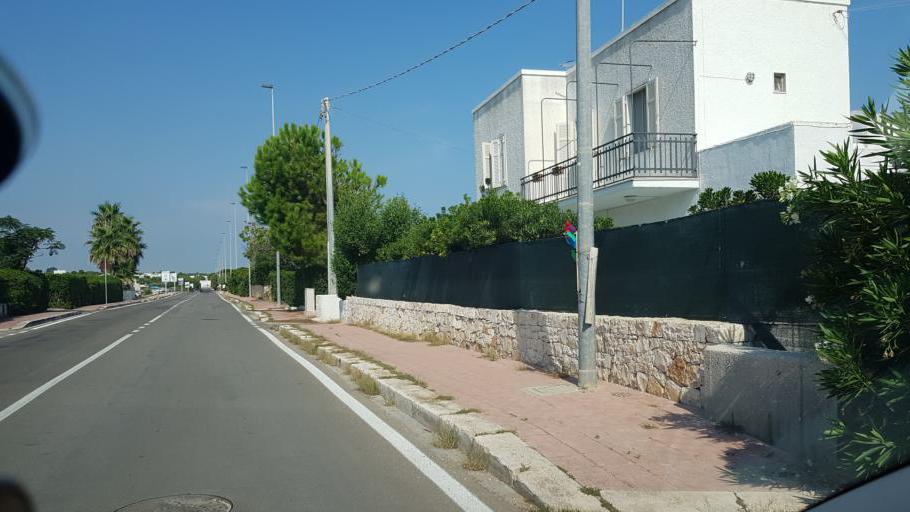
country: IT
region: Apulia
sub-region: Provincia di Brindisi
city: Fasano
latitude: 40.9016
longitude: 17.3576
